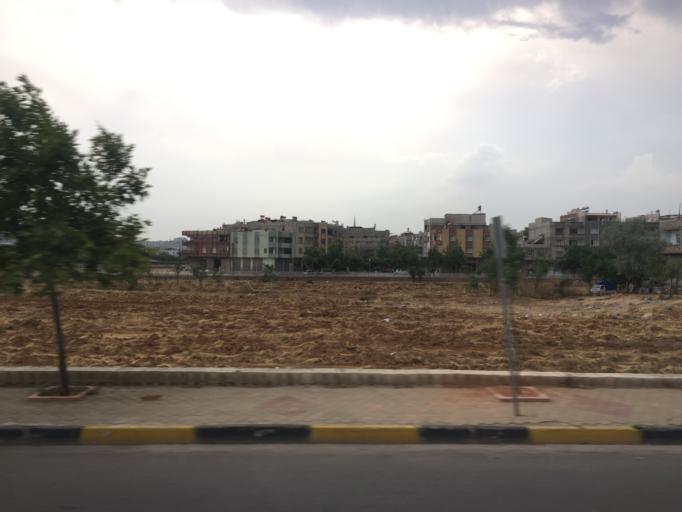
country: TR
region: Gaziantep
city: Gaziantep
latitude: 37.0619
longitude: 37.4155
